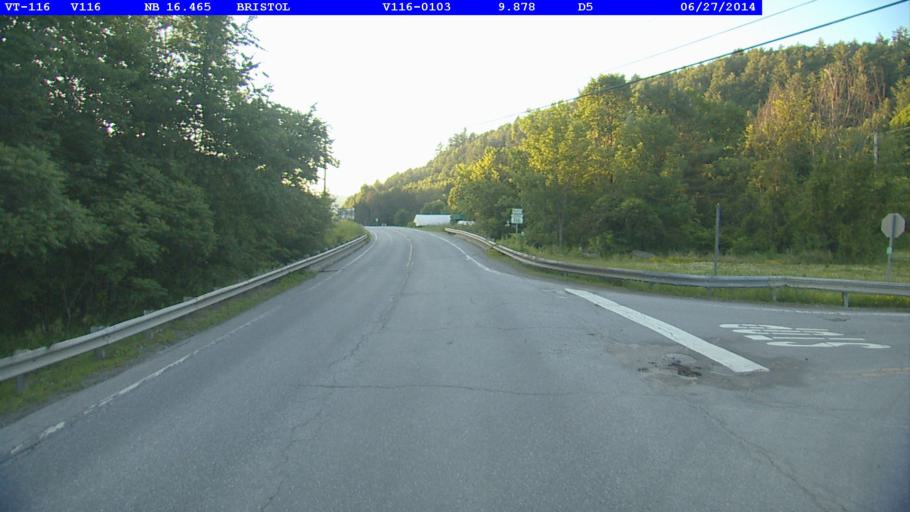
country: US
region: Vermont
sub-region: Addison County
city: Bristol
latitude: 44.1530
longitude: -73.0454
